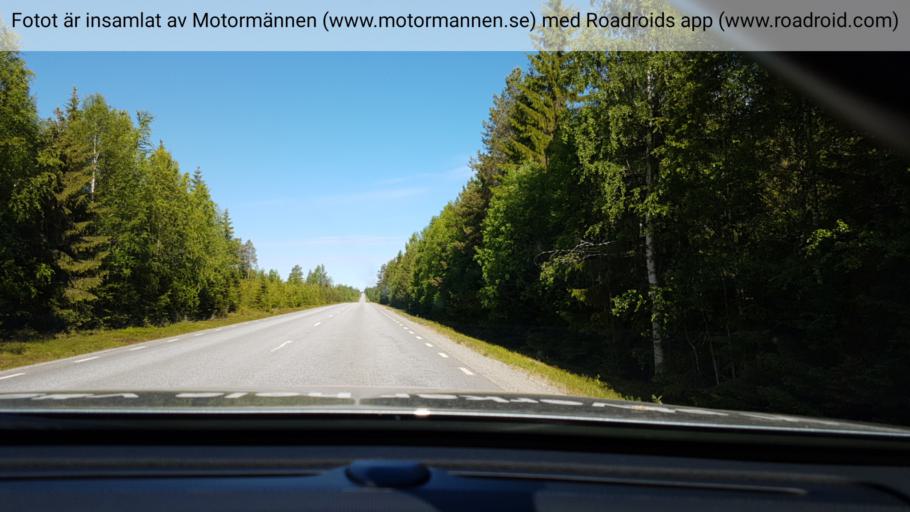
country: SE
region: Vaesterbotten
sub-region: Bjurholms Kommun
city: Bjurholm
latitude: 63.9420
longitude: 18.9242
